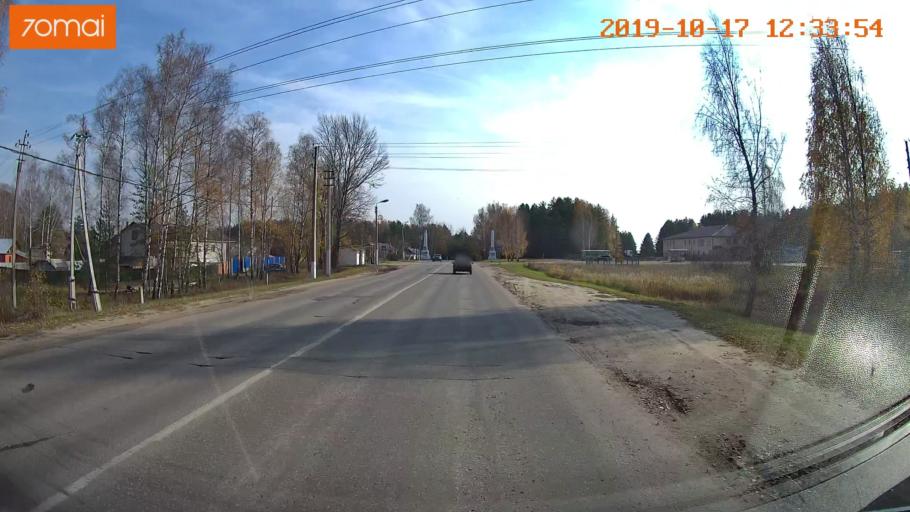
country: RU
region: Rjazan
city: Kasimov
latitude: 54.9513
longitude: 41.3590
